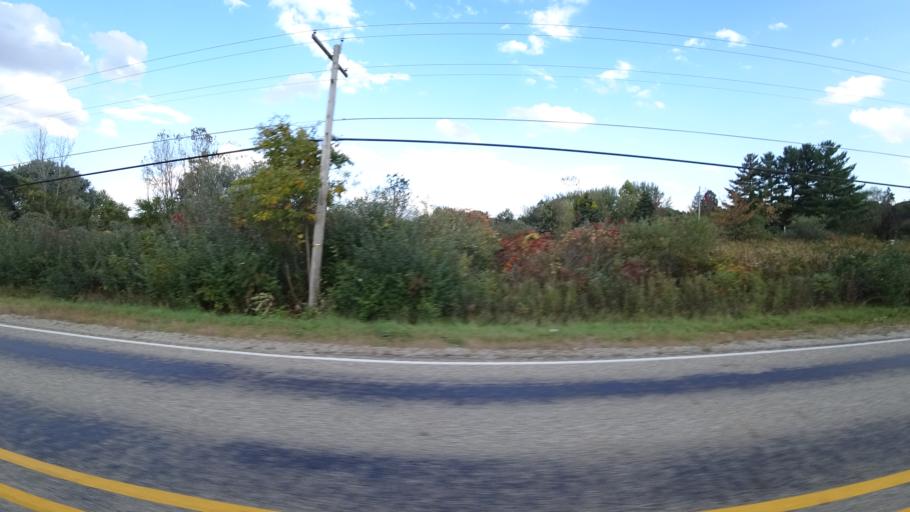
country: US
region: Michigan
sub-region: Saint Joseph County
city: Sturgis
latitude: 41.8339
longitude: -85.4285
